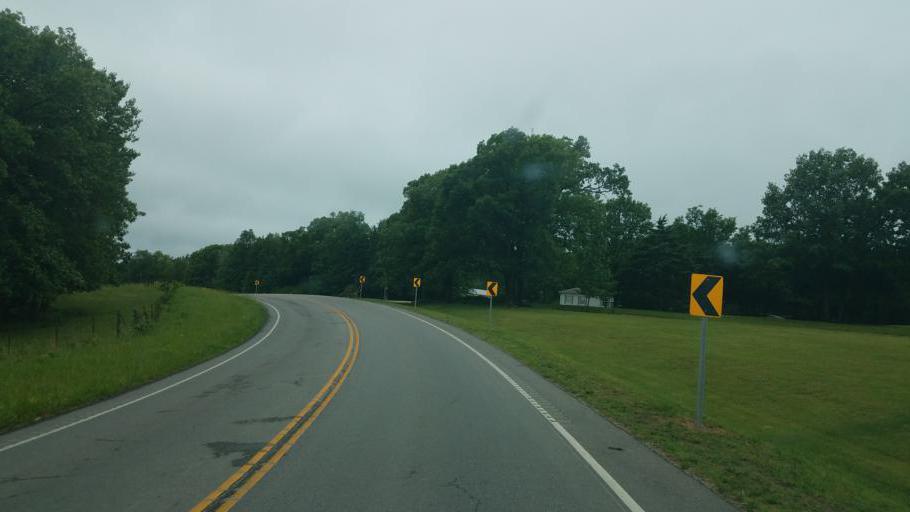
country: US
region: Missouri
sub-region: Moniteau County
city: California
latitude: 38.5431
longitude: -92.5744
